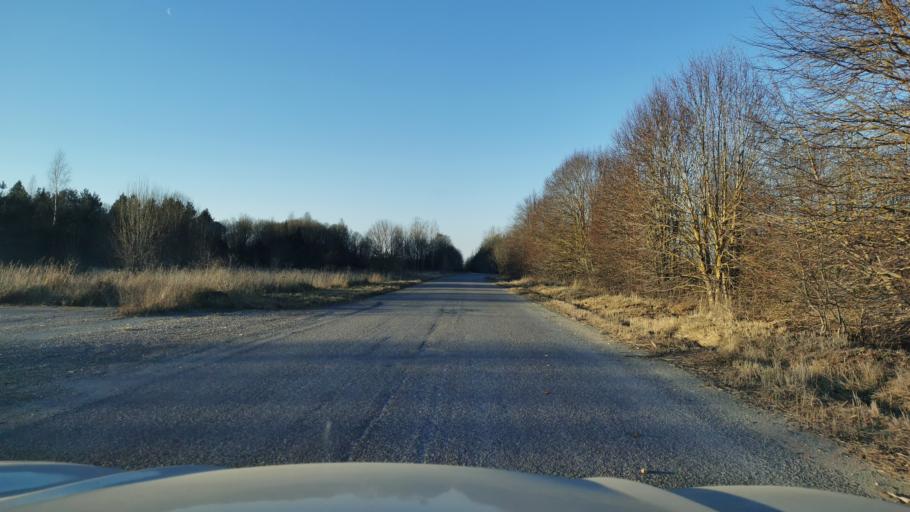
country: EE
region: Ida-Virumaa
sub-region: Puessi linn
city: Pussi
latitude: 59.3401
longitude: 27.0655
